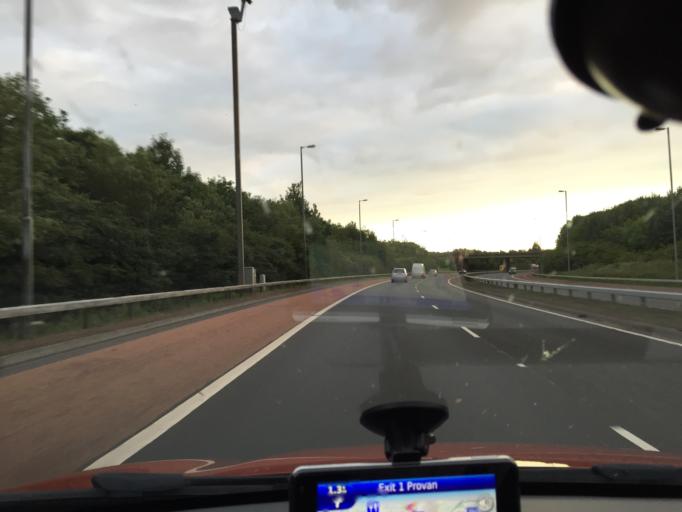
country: GB
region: Scotland
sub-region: North Lanarkshire
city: Stepps
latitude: 55.8836
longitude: -4.1861
